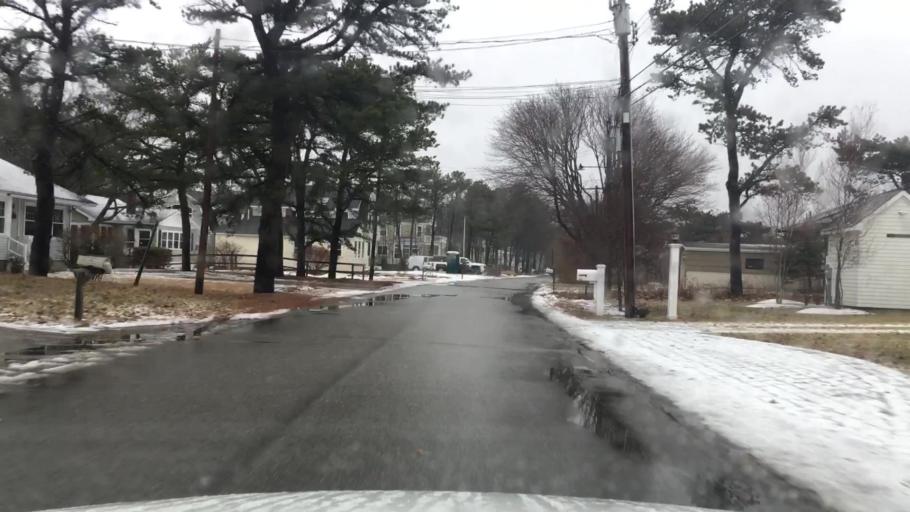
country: US
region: Maine
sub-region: York County
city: Arundel
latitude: 43.3941
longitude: -70.4240
